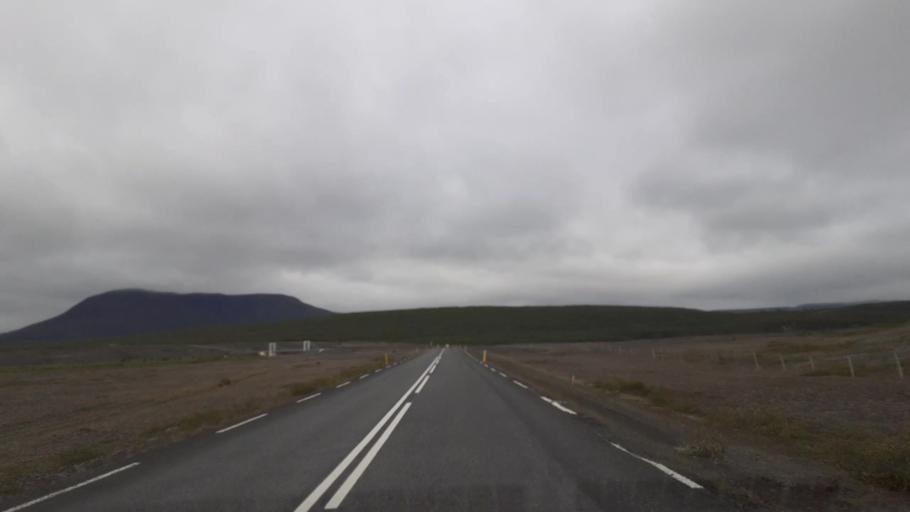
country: IS
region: Northeast
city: Husavik
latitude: 66.0306
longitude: -16.4636
